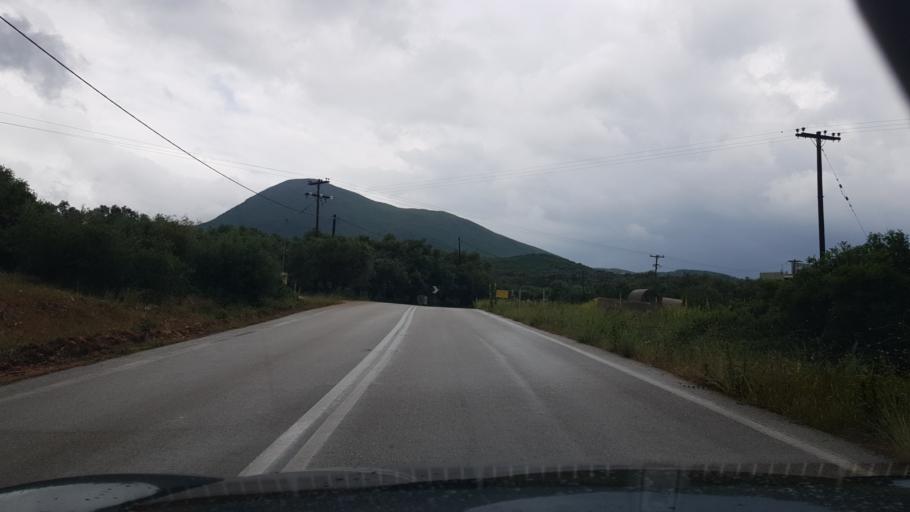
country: GR
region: Ionian Islands
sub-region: Lefkada
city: Nidri
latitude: 38.6339
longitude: 20.6708
